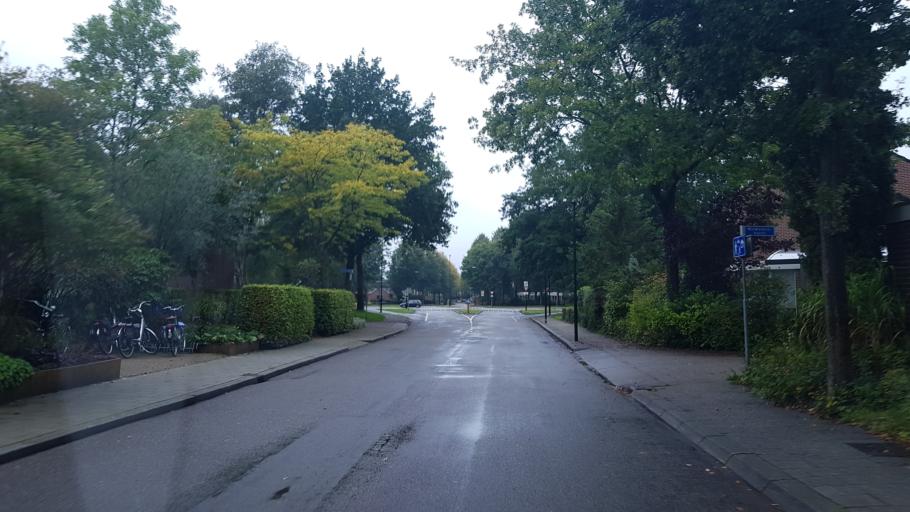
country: NL
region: Gelderland
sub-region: Gemeente Apeldoorn
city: Apeldoorn
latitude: 52.2045
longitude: 5.9904
